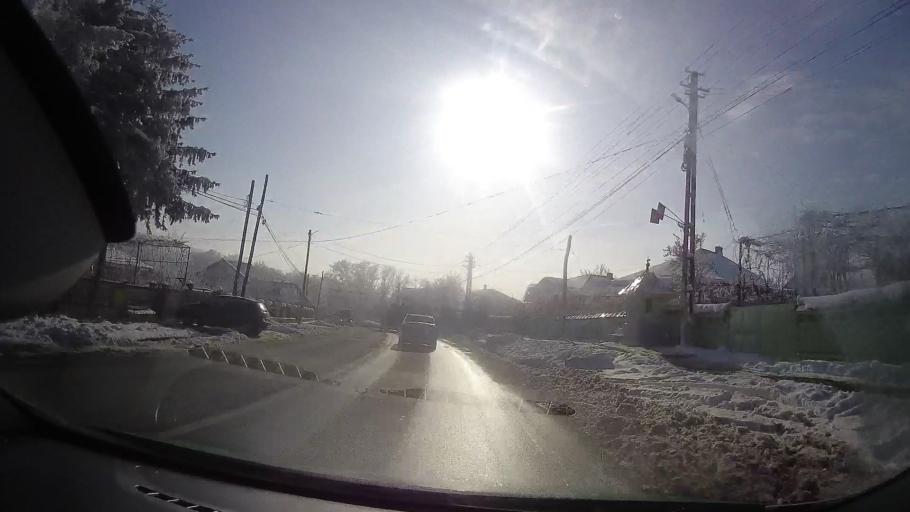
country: RO
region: Iasi
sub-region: Comuna Motca
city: Motca
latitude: 47.2371
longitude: 26.6033
